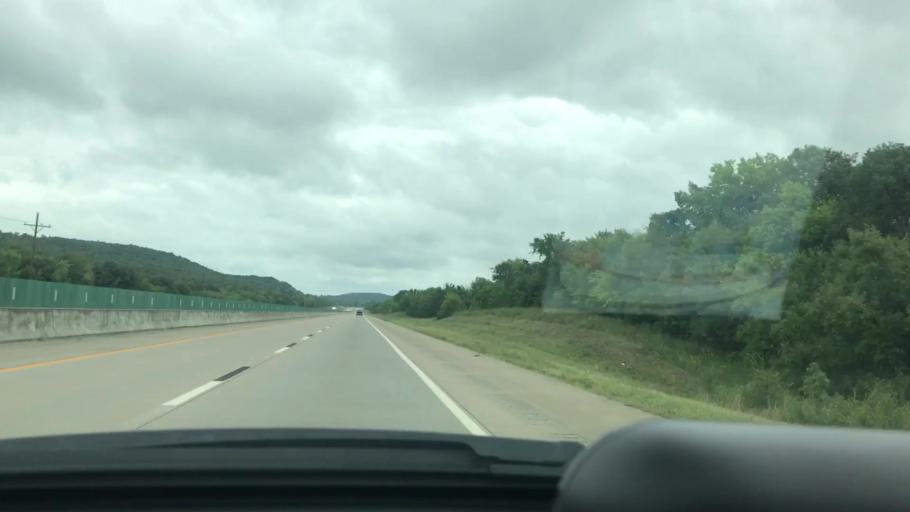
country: US
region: Oklahoma
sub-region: Pittsburg County
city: Krebs
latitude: 35.0768
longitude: -95.7034
